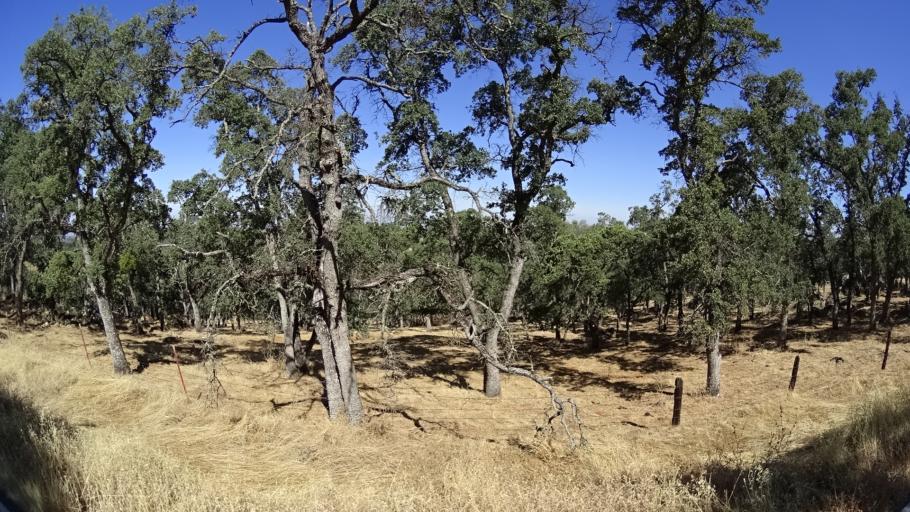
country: US
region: California
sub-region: Calaveras County
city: Valley Springs
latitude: 38.2502
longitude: -120.7779
